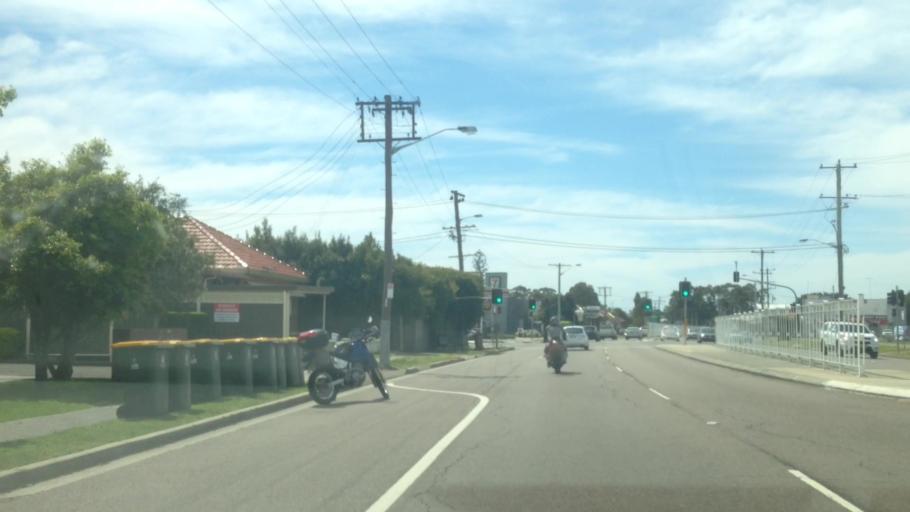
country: AU
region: New South Wales
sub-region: Newcastle
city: Broadmeadow
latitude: -32.9188
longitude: 151.7242
